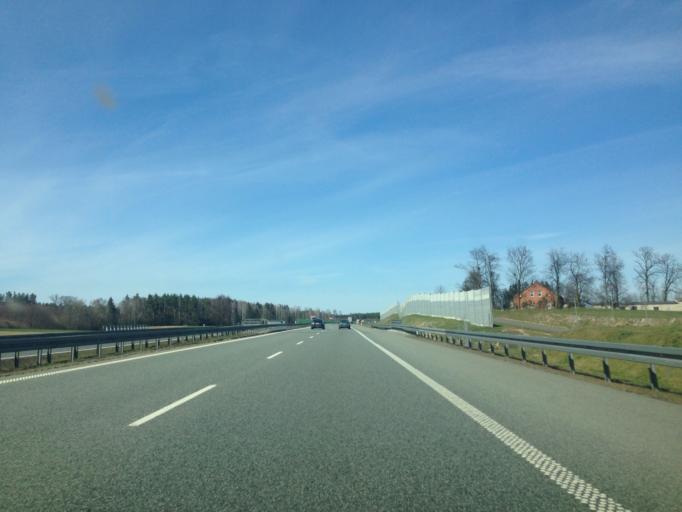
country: PL
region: Pomeranian Voivodeship
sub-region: Powiat starogardzki
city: Bobowo
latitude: 53.8716
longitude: 18.6286
